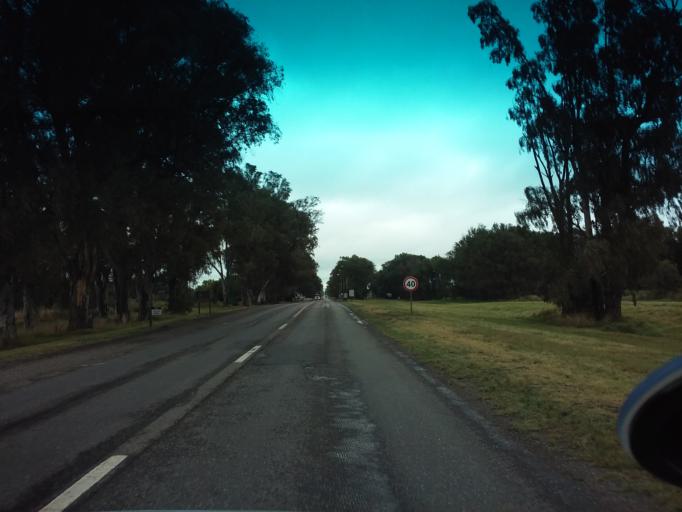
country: AR
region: La Pampa
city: Catrilo
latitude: -36.4102
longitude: -63.3831
